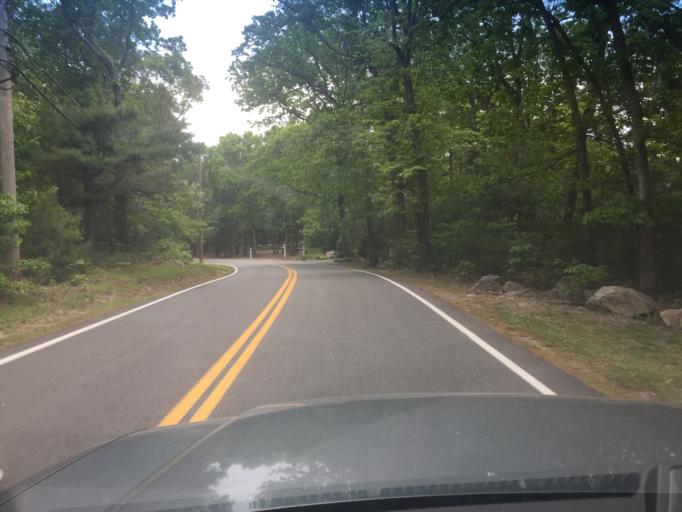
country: US
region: Massachusetts
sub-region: Norfolk County
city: Westwood
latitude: 42.2064
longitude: -71.2606
